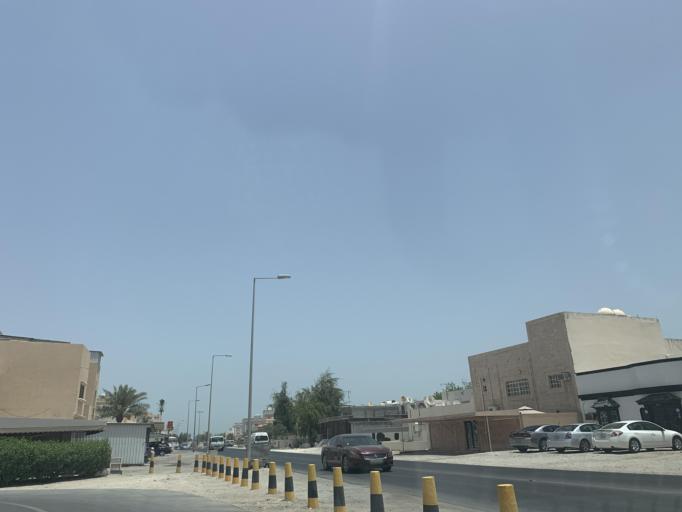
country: BH
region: Northern
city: Madinat `Isa
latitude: 26.1664
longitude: 50.5668
